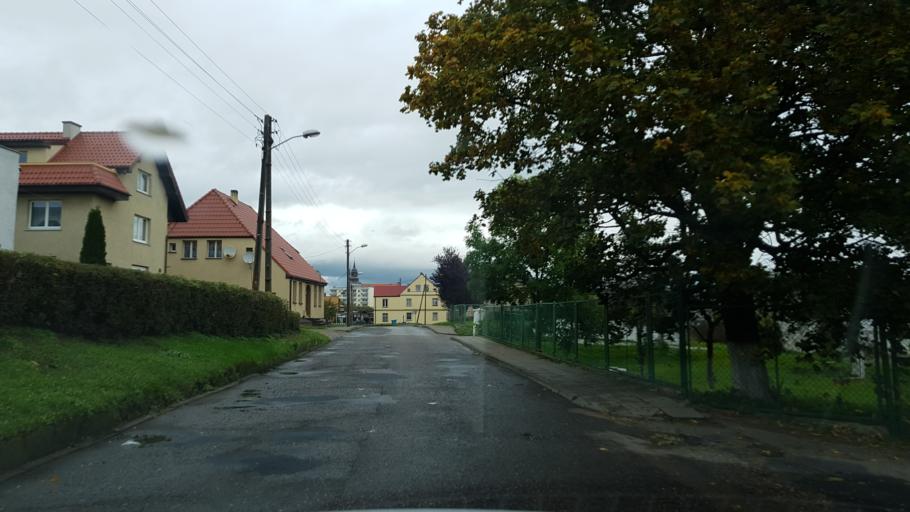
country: PL
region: West Pomeranian Voivodeship
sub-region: Powiat kamienski
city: Wolin
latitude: 53.8378
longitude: 14.6148
